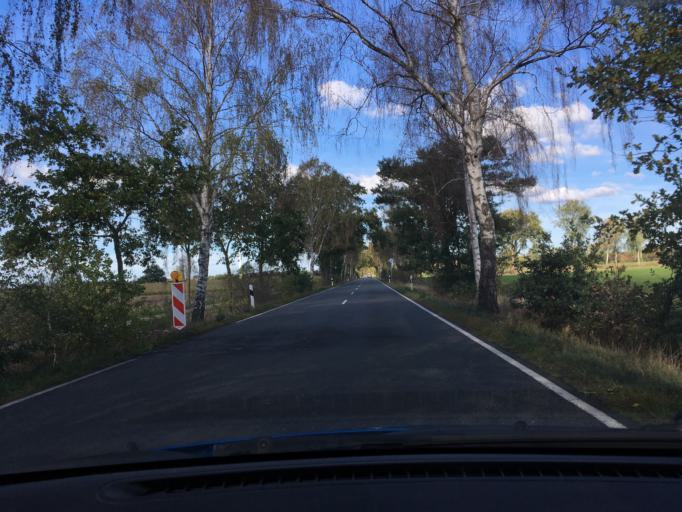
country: DE
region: Lower Saxony
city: Isernhagen Farster Bauerschaft
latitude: 52.5472
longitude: 9.8546
